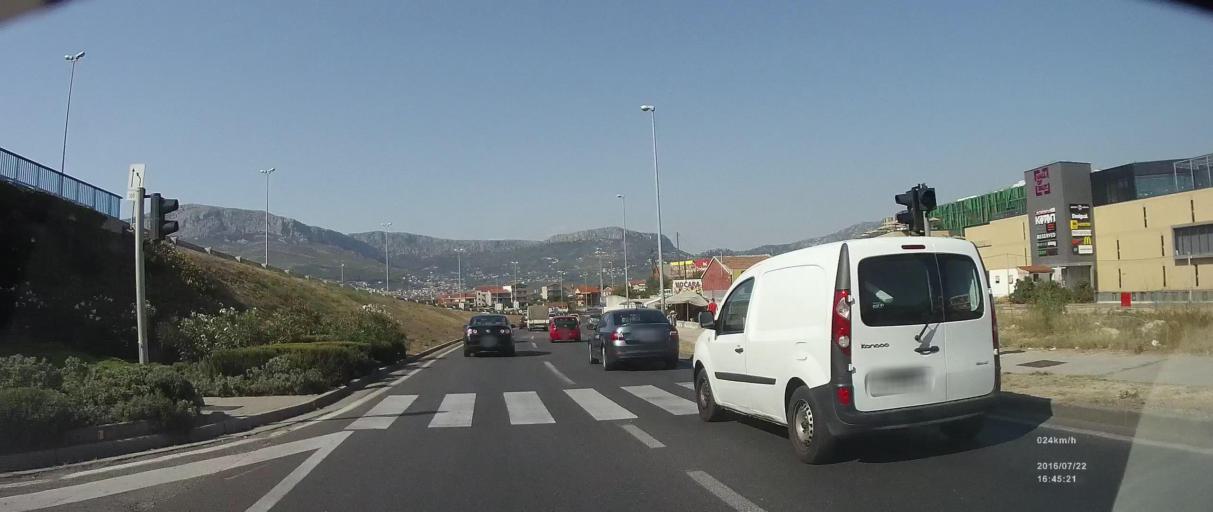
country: HR
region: Splitsko-Dalmatinska
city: Vranjic
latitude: 43.5185
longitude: 16.4813
